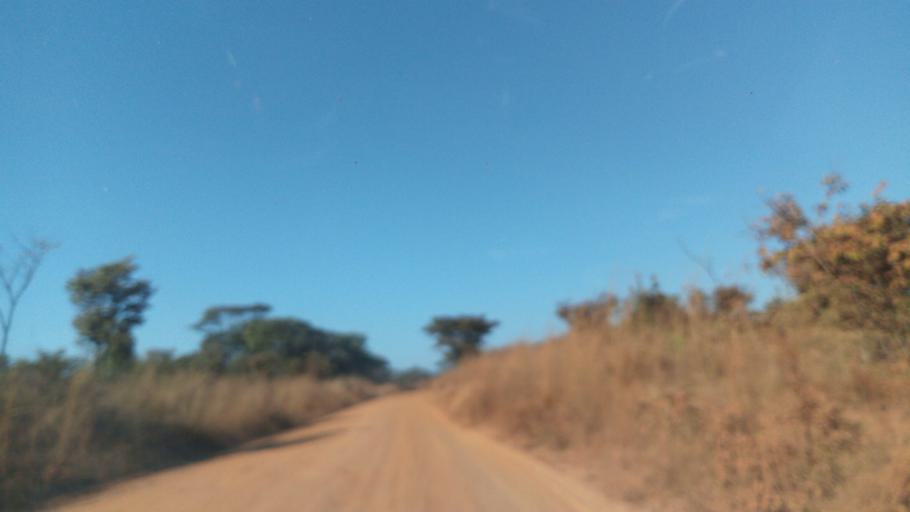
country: ZM
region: Luapula
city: Mwense
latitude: -10.6445
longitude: 28.4095
